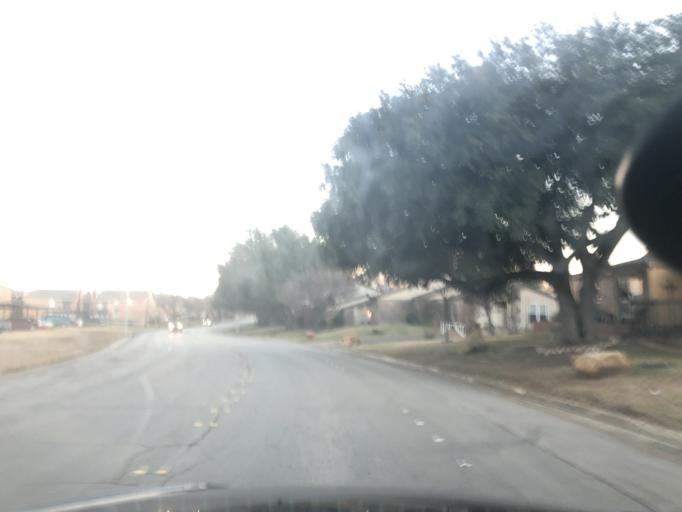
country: US
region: Texas
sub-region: Tarrant County
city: White Settlement
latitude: 32.7326
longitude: -97.4719
